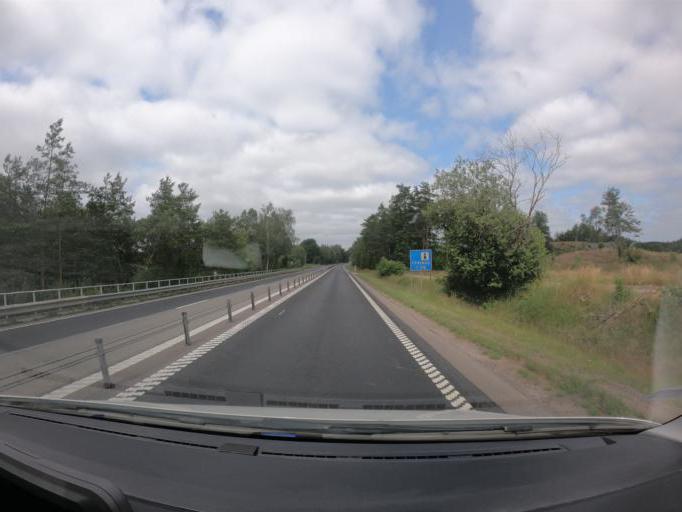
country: SE
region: Skane
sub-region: Perstorps Kommun
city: Perstorp
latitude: 56.1484
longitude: 13.5382
